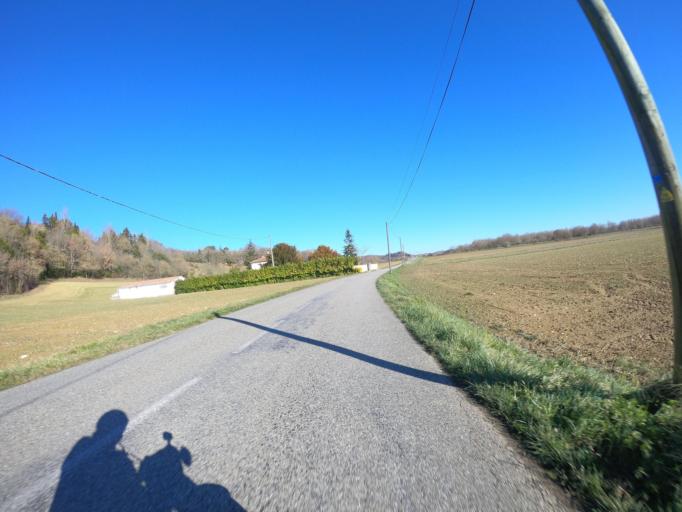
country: FR
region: Midi-Pyrenees
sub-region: Departement de l'Ariege
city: Mirepoix
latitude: 43.0926
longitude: 1.8424
